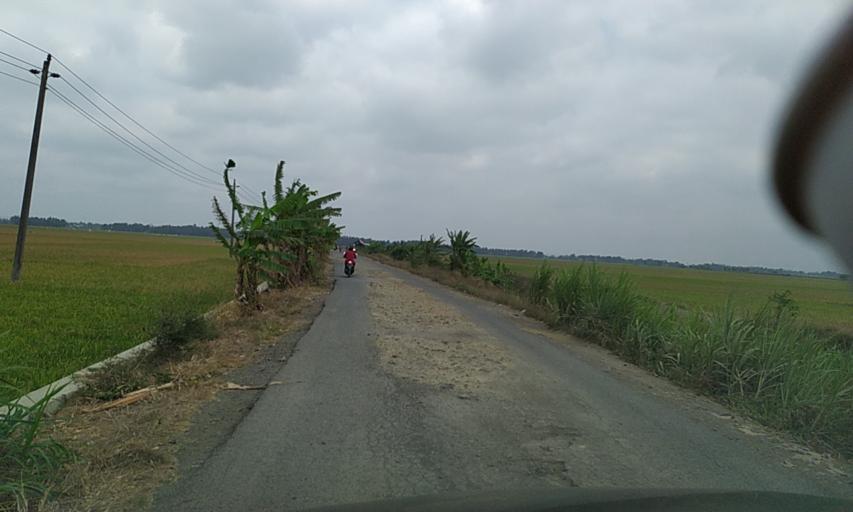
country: ID
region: Central Java
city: Sidakaya
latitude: -7.6161
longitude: 108.9276
